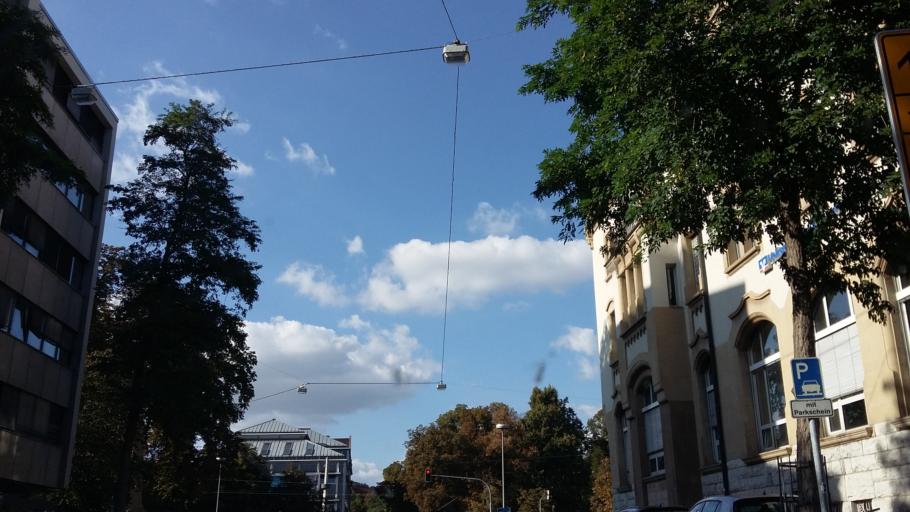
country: DE
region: Baden-Wuerttemberg
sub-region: Tuebingen Region
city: Ulm
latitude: 48.4018
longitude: 9.9969
